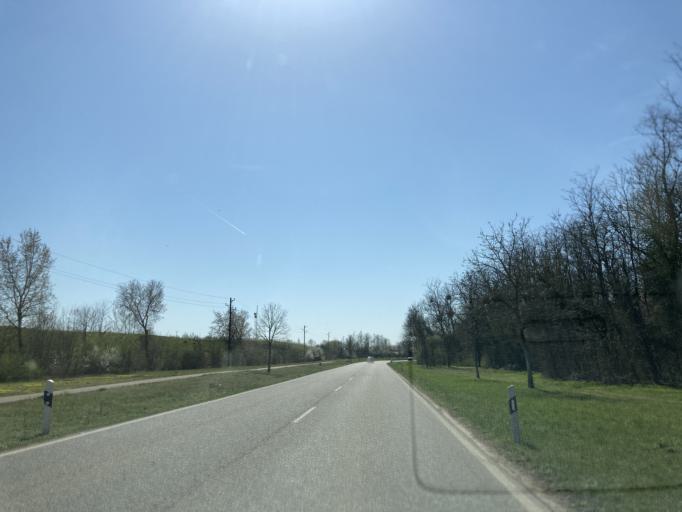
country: DE
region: Baden-Wuerttemberg
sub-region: Freiburg Region
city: Hartheim
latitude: 47.9029
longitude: 7.5993
